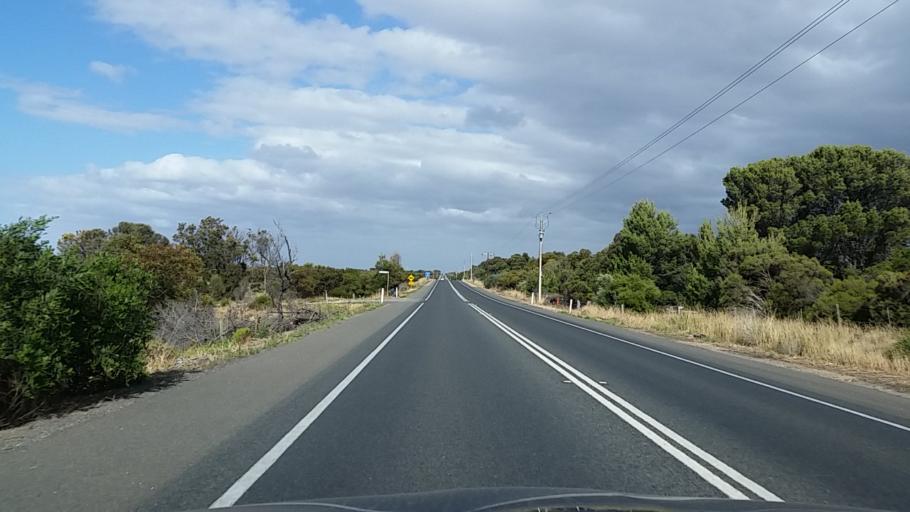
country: AU
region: South Australia
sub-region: Alexandrina
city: Goolwa
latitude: -35.5073
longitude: 138.7479
